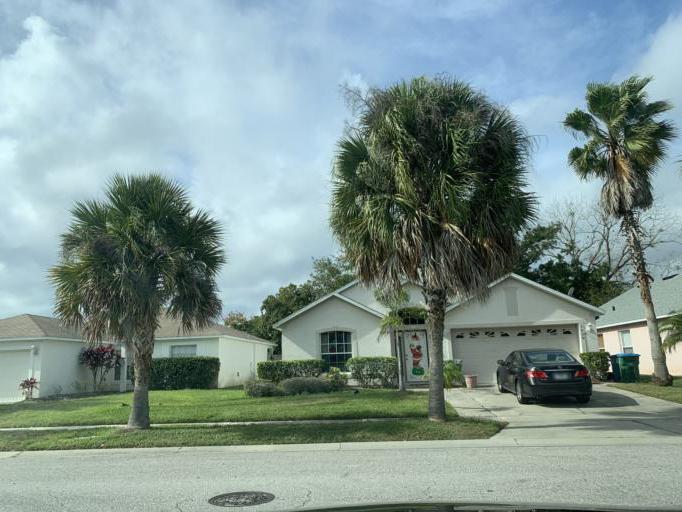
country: US
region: Florida
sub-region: Orange County
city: Eatonville
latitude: 28.6284
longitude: -81.4074
